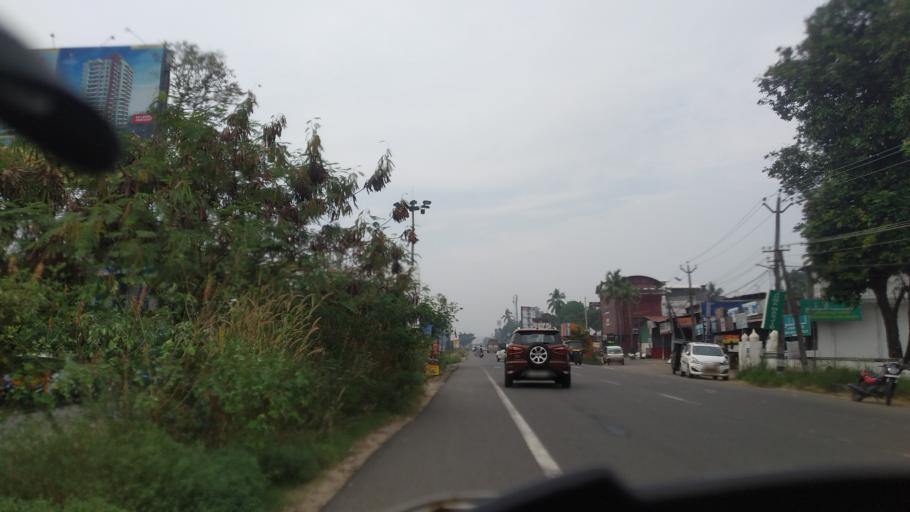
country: IN
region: Kerala
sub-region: Ernakulam
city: Elur
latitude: 10.0505
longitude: 76.2940
